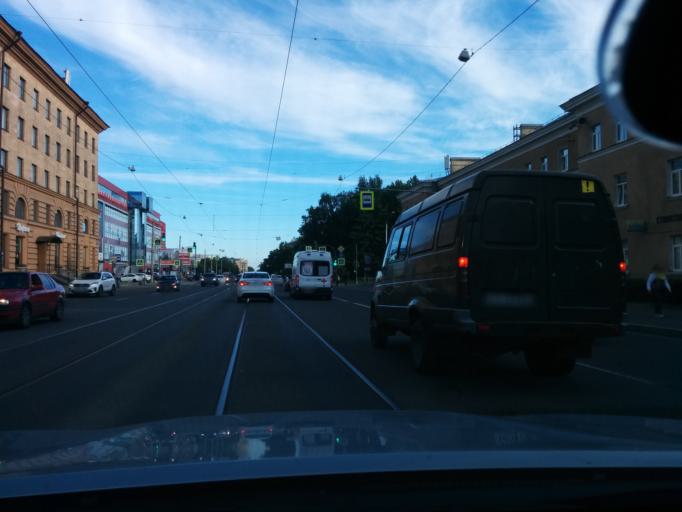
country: RU
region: Leningrad
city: Udel'naya
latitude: 60.0118
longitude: 30.3243
